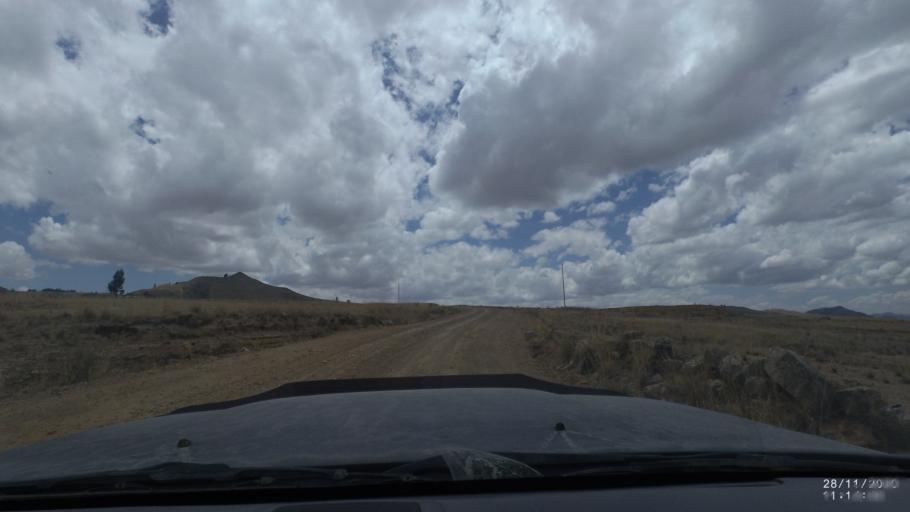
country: BO
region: Cochabamba
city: Tarata
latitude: -17.7456
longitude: -66.0956
